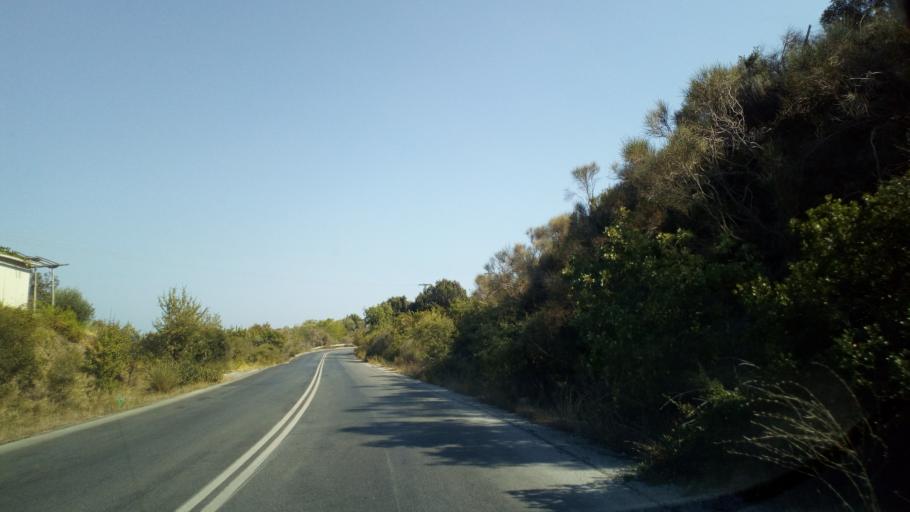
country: GR
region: Central Macedonia
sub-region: Nomos Thessalonikis
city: Stavros
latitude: 40.6206
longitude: 23.7718
